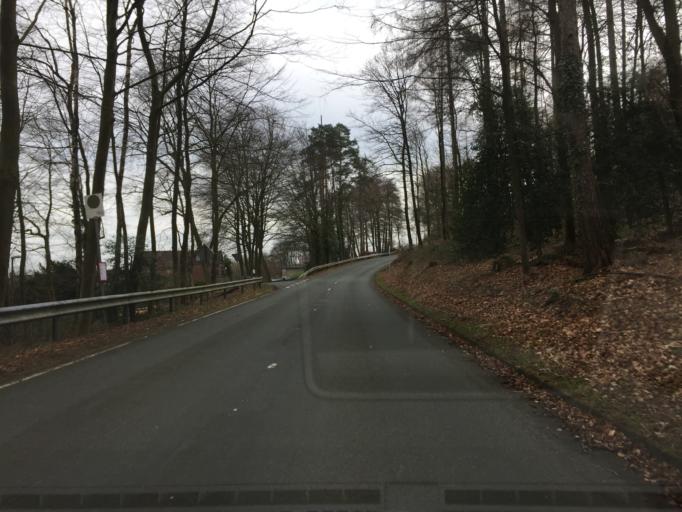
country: DE
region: North Rhine-Westphalia
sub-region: Regierungsbezirk Detmold
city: Detmold
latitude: 51.9190
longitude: 8.8398
